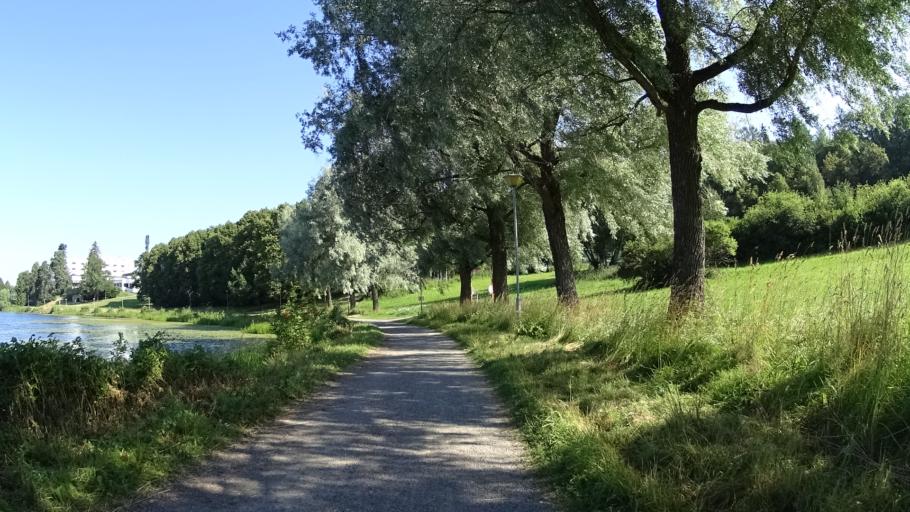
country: FI
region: Haeme
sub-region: Haemeenlinna
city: Haemeenlinna
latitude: 61.0196
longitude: 24.4470
